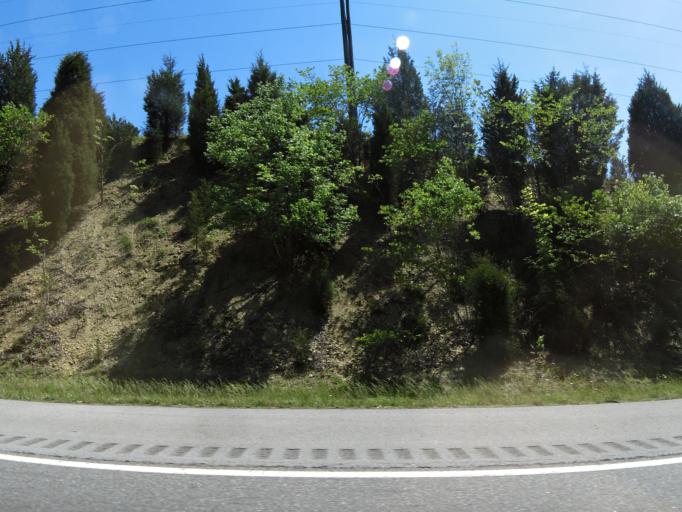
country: US
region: Tennessee
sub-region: Knox County
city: Mascot
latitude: 35.9868
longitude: -83.6523
